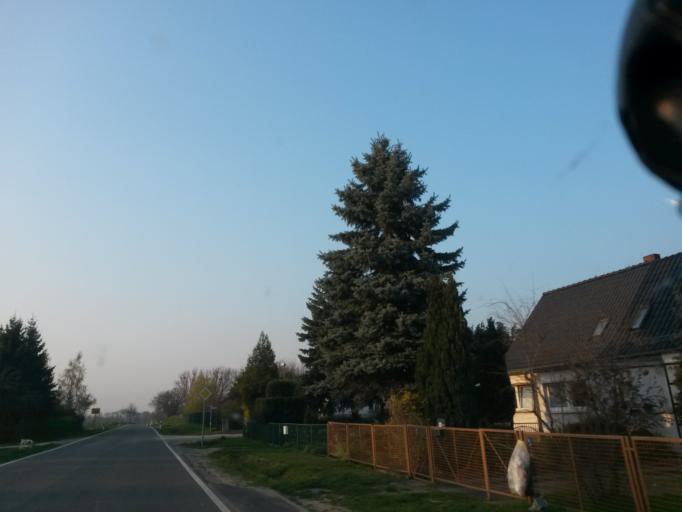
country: DE
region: Brandenburg
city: Buckow
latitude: 52.6225
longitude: 14.0696
